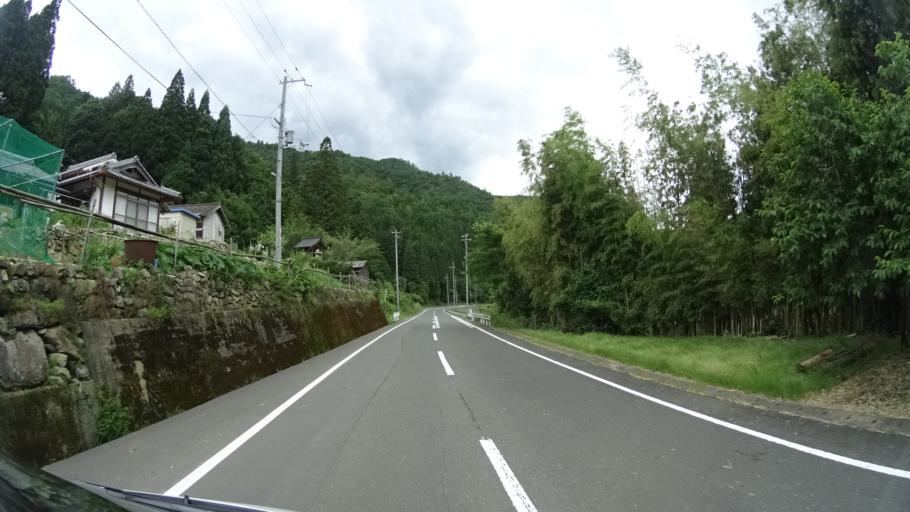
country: JP
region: Hyogo
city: Sasayama
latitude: 35.0567
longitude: 135.3937
